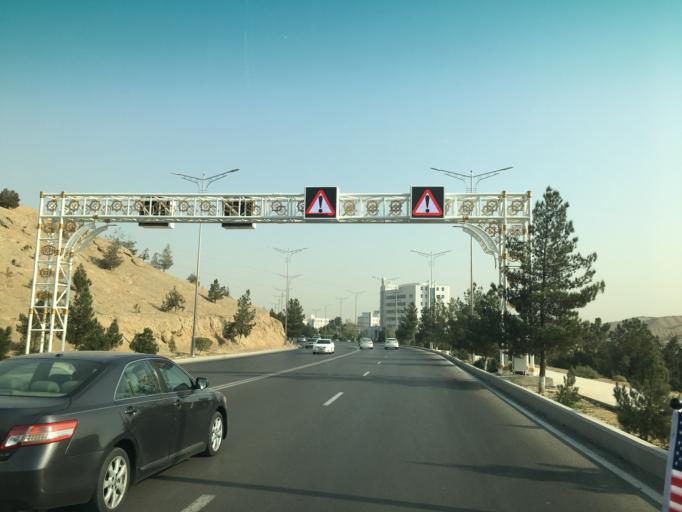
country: TM
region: Ahal
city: Ashgabat
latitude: 37.9411
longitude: 58.3263
